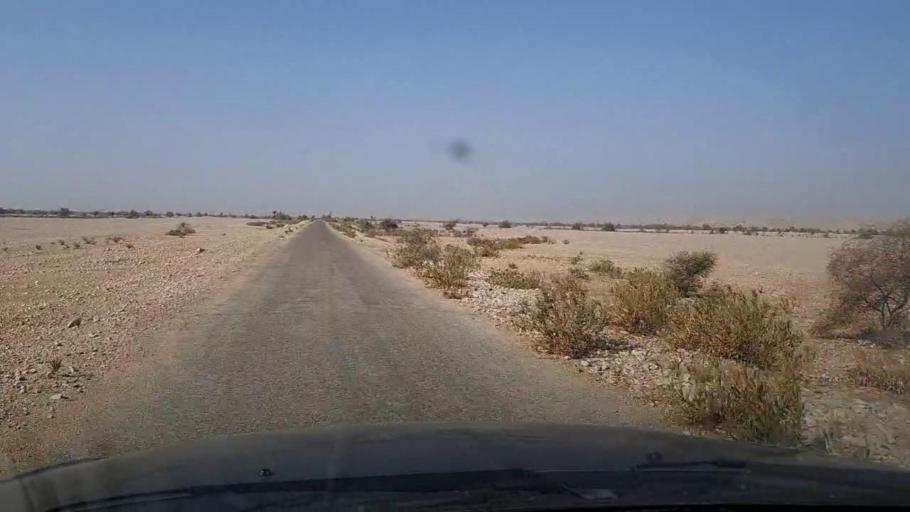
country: PK
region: Sindh
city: Sann
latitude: 25.8958
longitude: 67.9944
